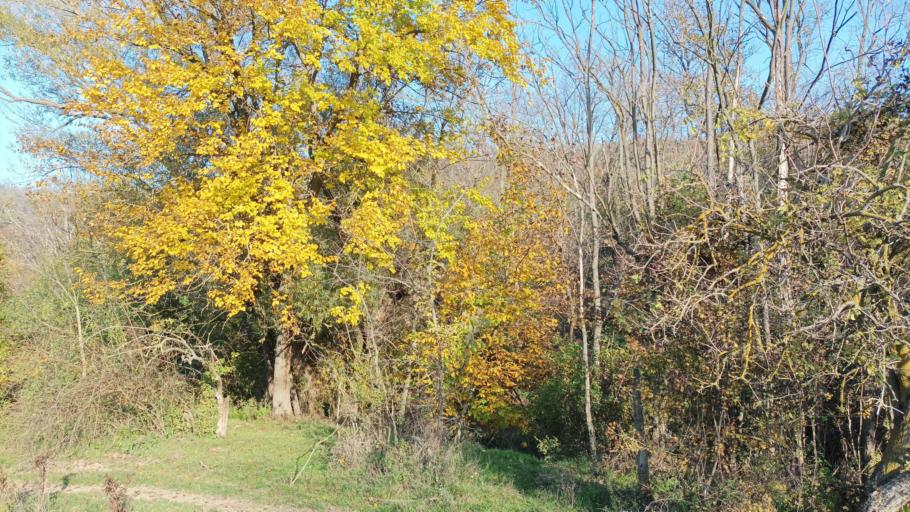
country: HU
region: Tolna
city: Szentgalpuszta
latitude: 46.3328
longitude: 18.6070
